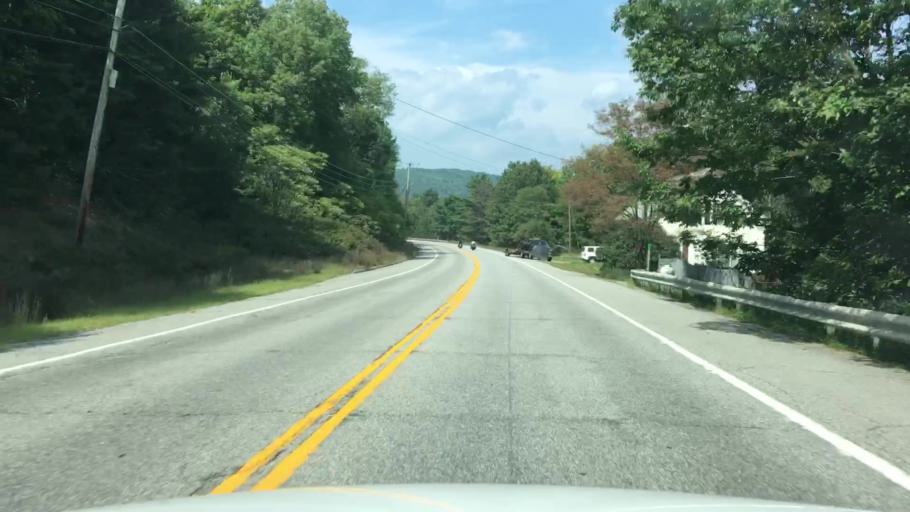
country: US
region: Maine
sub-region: Oxford County
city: Peru
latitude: 44.5027
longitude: -70.4007
